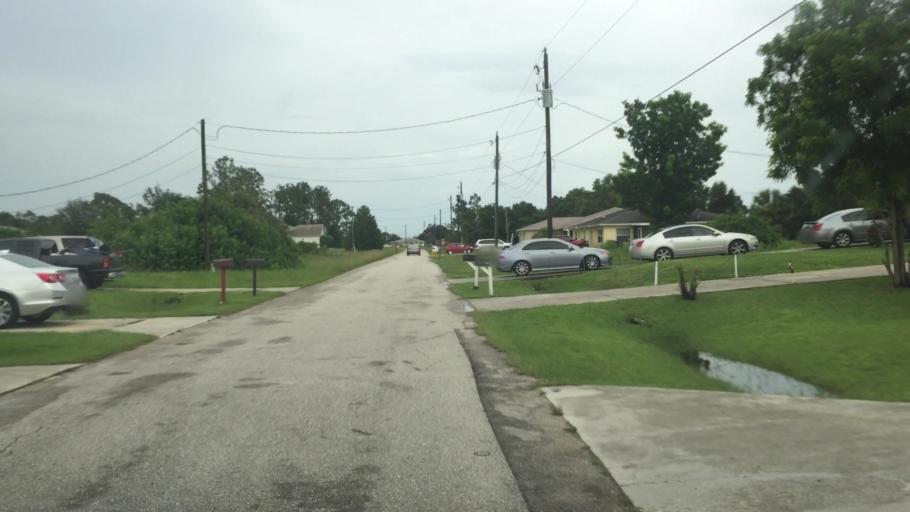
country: US
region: Florida
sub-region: Lee County
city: Gateway
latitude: 26.5903
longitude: -81.7201
